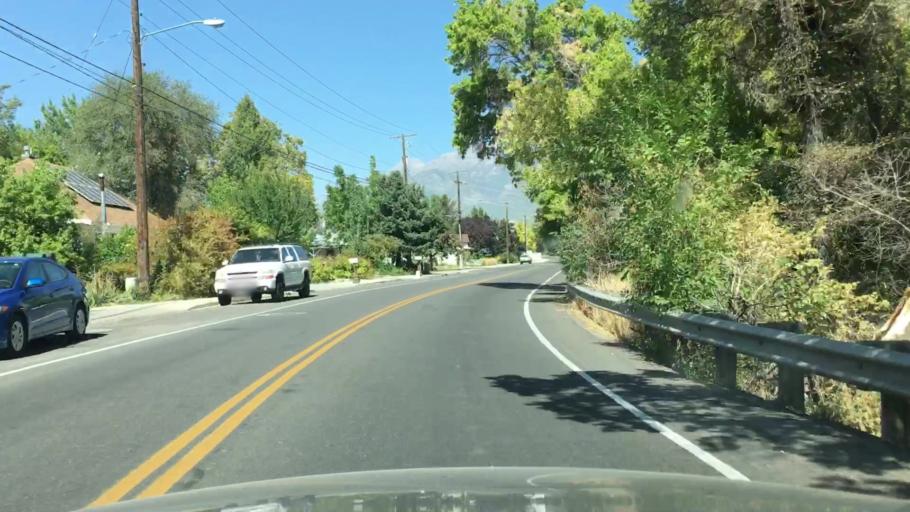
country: US
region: Utah
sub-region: Utah County
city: Provo
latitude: 40.2604
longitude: -111.6717
